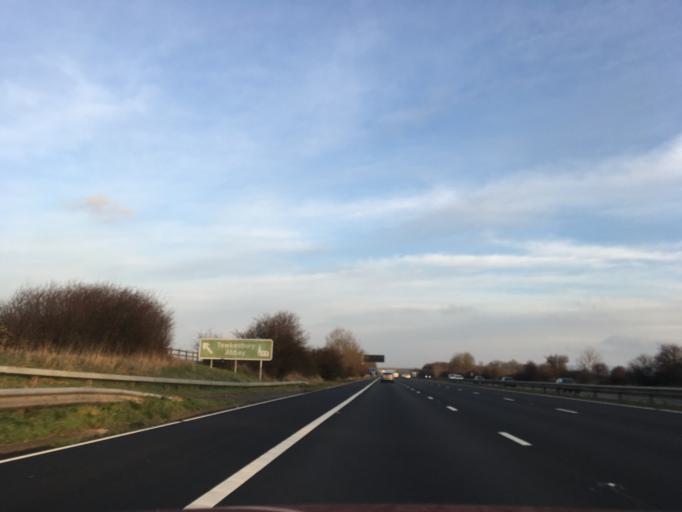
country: GB
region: England
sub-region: Gloucestershire
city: Tewkesbury
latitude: 51.9795
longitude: -2.1266
